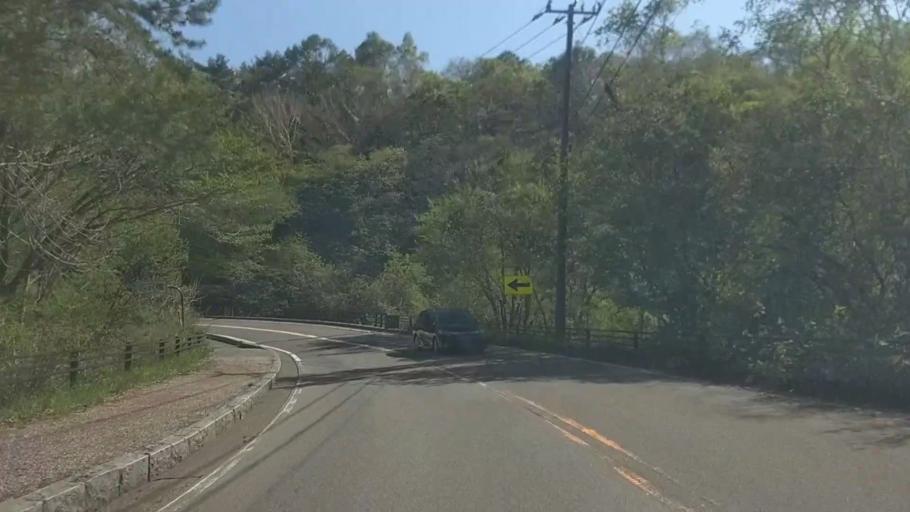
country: JP
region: Yamanashi
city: Nirasaki
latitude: 35.9225
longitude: 138.4053
